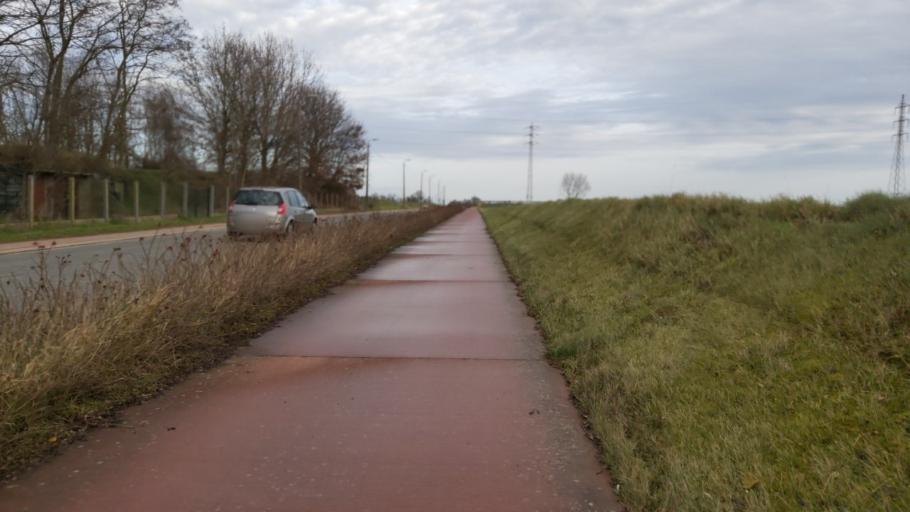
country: BE
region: Flanders
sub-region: Provincie Vlaams-Brabant
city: Tienen
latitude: 50.8277
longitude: 4.9003
